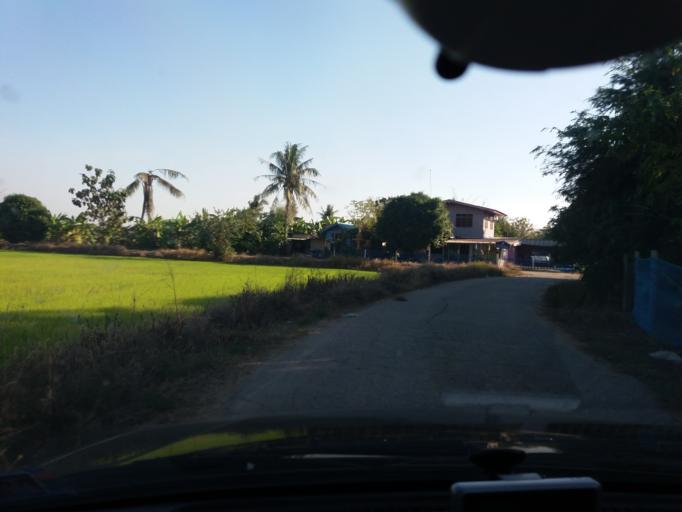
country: TH
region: Suphan Buri
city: Doem Bang Nang Buat
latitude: 14.9074
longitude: 100.1320
